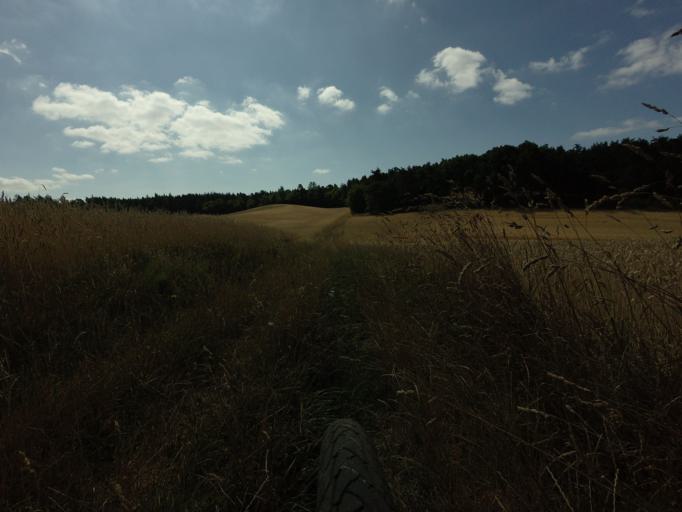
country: DK
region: Central Jutland
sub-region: Odder Kommune
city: Odder
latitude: 55.8952
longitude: 10.0718
